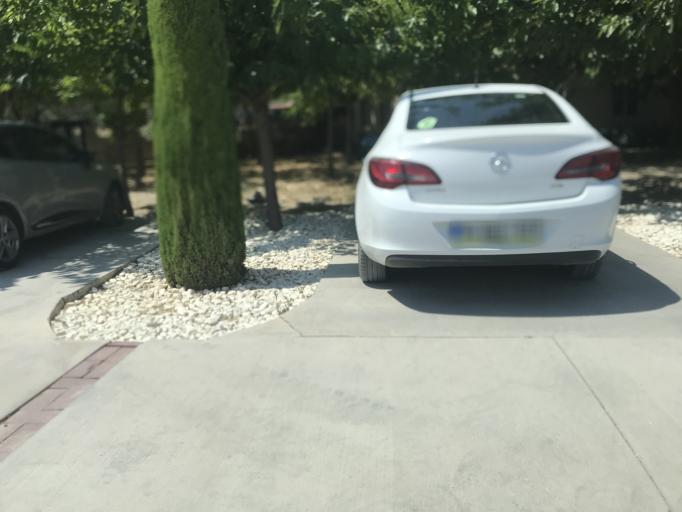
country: TR
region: Izmir
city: Urla
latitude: 38.2525
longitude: 26.7361
